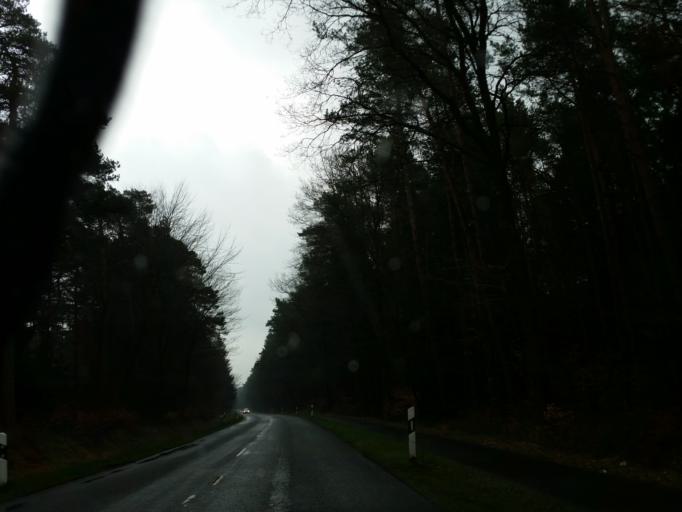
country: DE
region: Lower Saxony
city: Hipstedt
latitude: 53.4985
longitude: 9.0032
